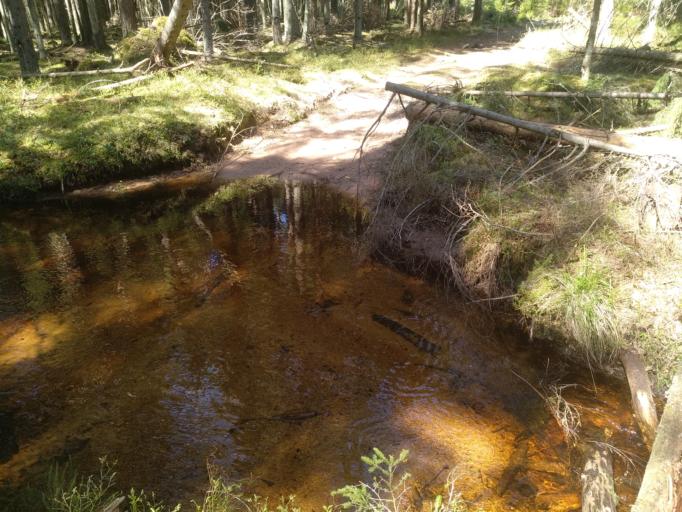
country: RU
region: Leningrad
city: Yakovlevo
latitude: 60.4302
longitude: 29.4246
